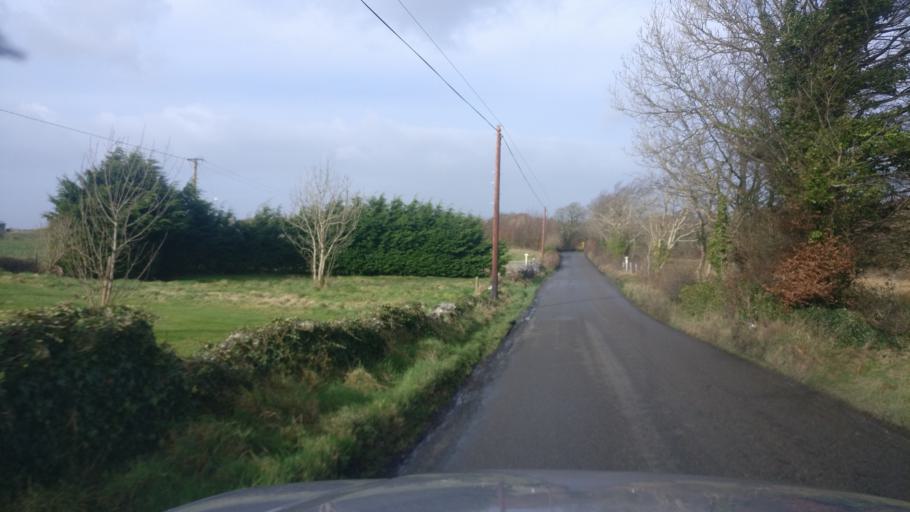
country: IE
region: Connaught
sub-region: County Galway
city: Loughrea
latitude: 53.2801
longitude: -8.5840
